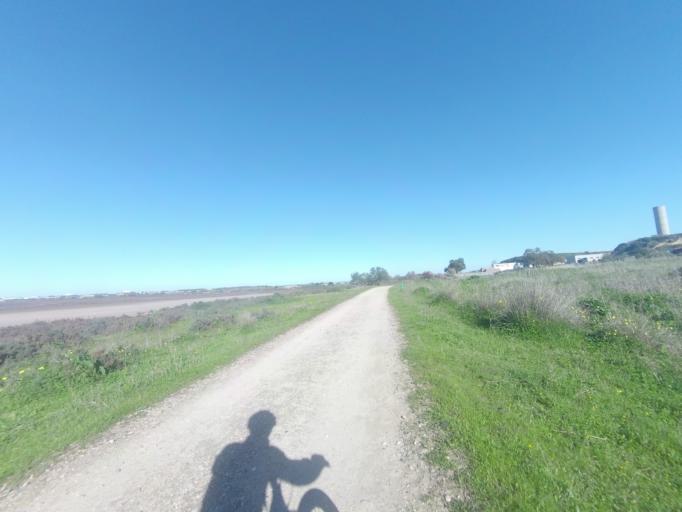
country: ES
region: Andalusia
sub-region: Provincia de Huelva
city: Palos de la Frontera
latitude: 37.2422
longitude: -6.8889
